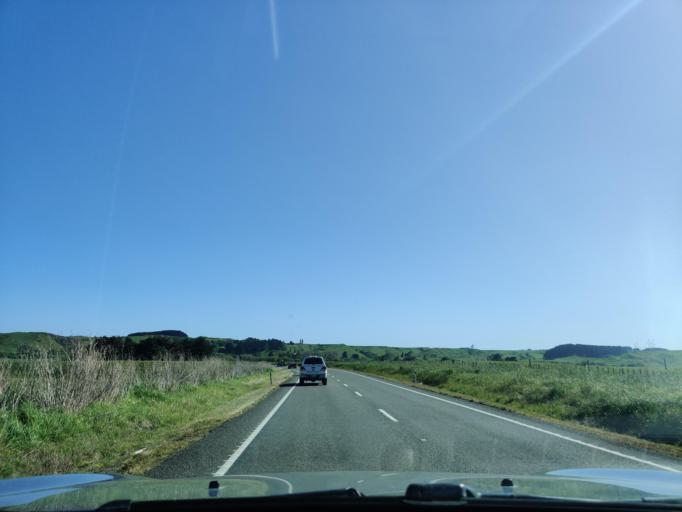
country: NZ
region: Manawatu-Wanganui
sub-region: Wanganui District
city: Wanganui
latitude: -40.0143
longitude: 175.1730
